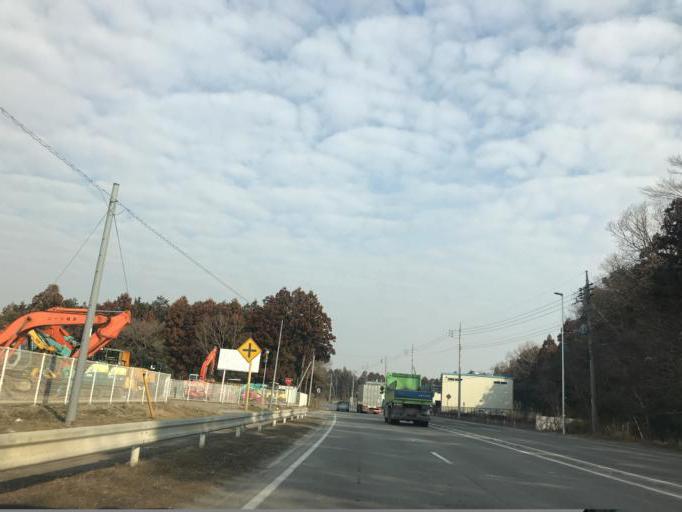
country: JP
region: Ibaraki
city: Ishige
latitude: 36.0867
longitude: 140.0389
